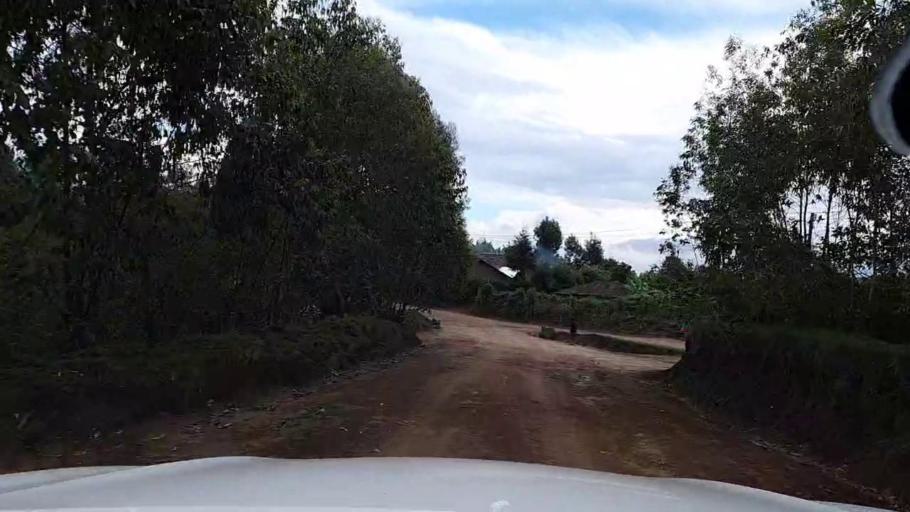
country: BI
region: Kayanza
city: Kayanza
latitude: -2.7991
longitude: 29.5027
